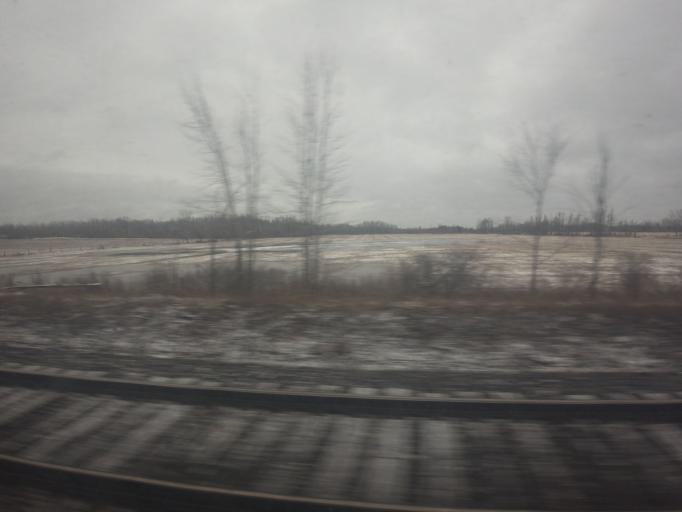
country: CA
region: Ontario
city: Gananoque
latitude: 44.3711
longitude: -76.1322
